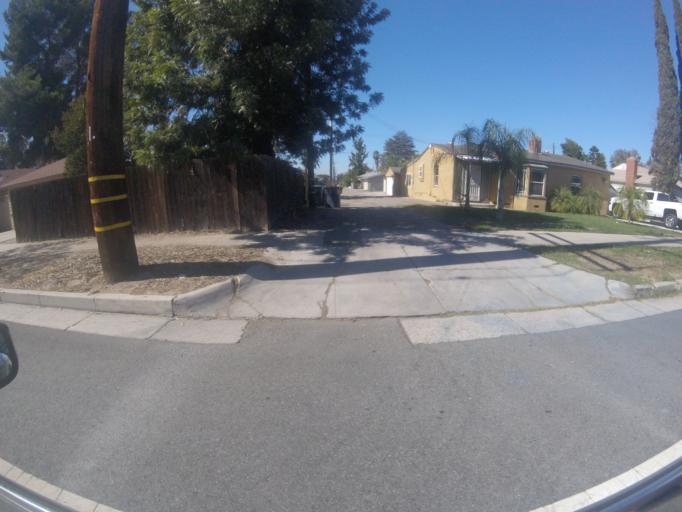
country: US
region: California
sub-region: San Bernardino County
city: Redlands
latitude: 34.0633
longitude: -117.1738
